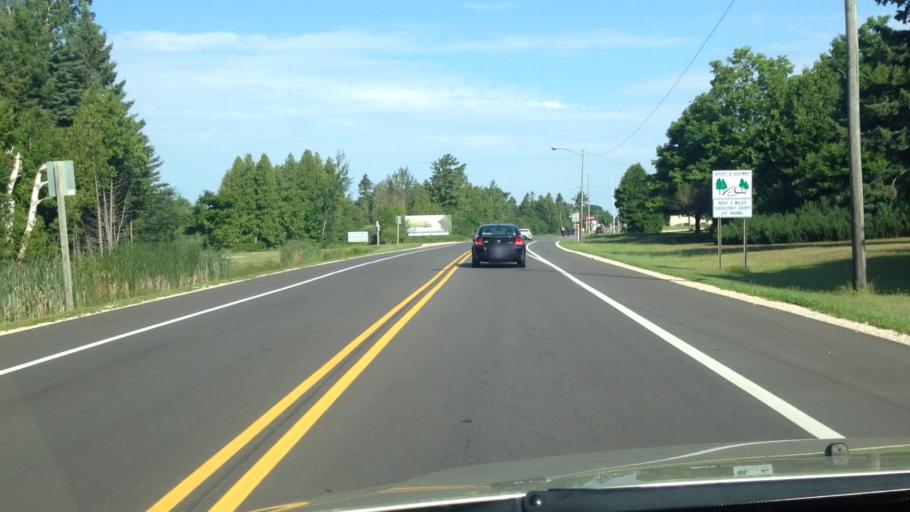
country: US
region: Michigan
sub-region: Schoolcraft County
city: Manistique
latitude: 45.9484
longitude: -86.2393
